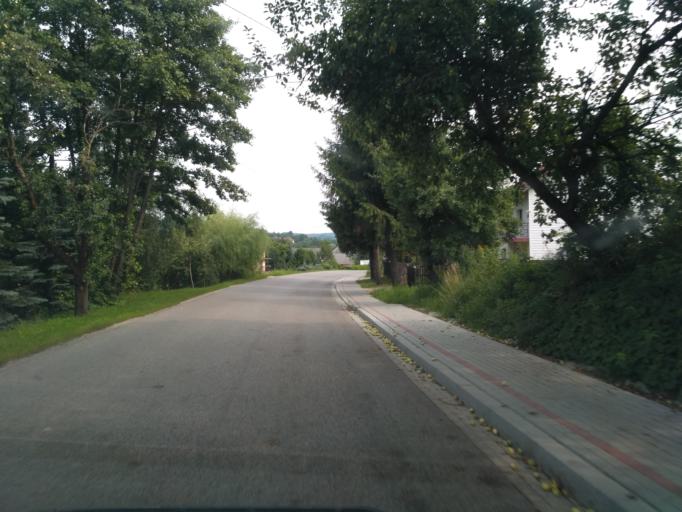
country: PL
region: Subcarpathian Voivodeship
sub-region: Powiat strzyzowski
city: Niebylec
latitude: 49.8526
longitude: 21.9134
